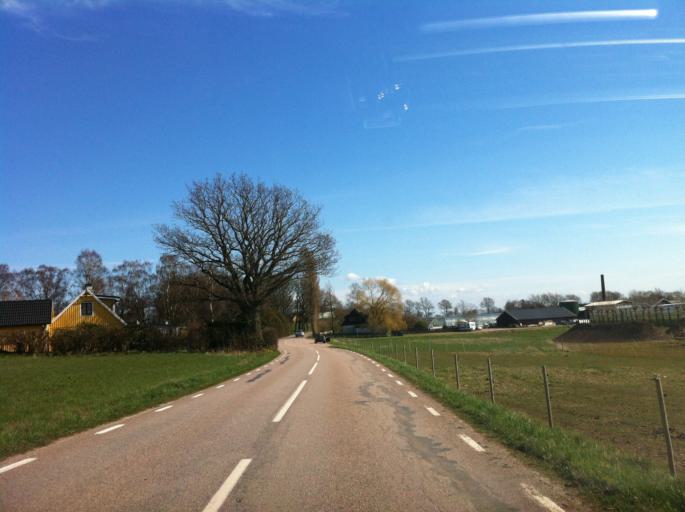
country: SE
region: Skane
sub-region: Hoganas Kommun
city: Hoganas
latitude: 56.2670
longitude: 12.5511
